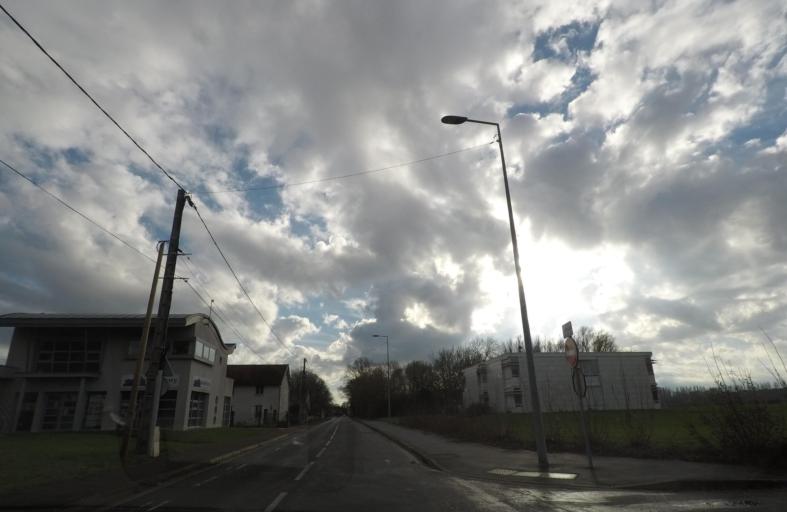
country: FR
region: Centre
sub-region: Departement du Cher
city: Bourges
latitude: 47.0571
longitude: 2.4039
